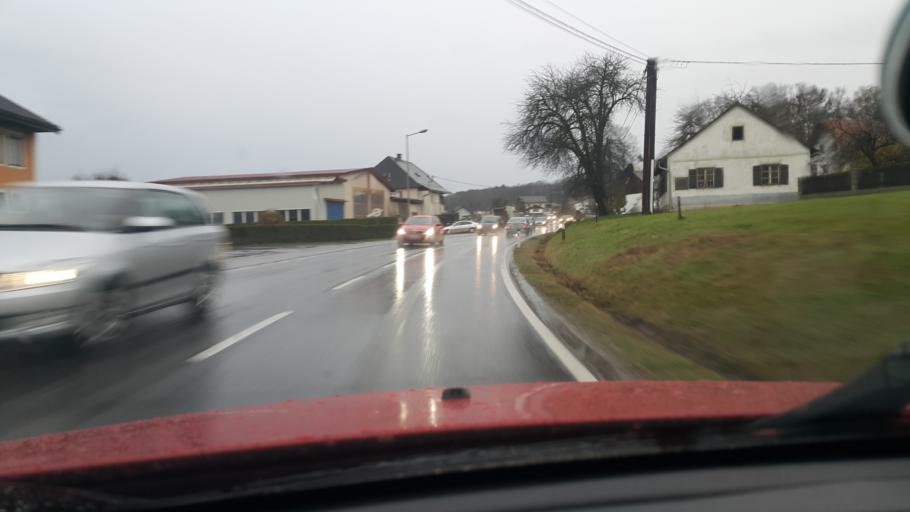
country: AT
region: Styria
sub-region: Politischer Bezirk Leibnitz
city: Weitendorf
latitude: 46.8667
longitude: 15.4744
